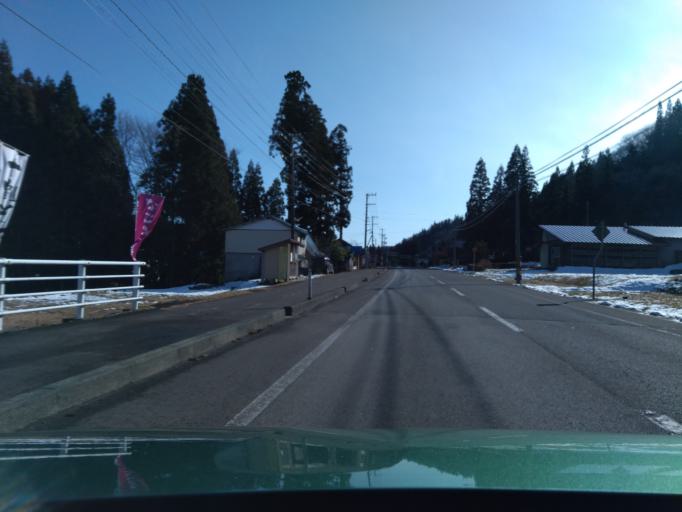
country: JP
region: Iwate
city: Hanamaki
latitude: 39.4495
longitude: 141.0037
